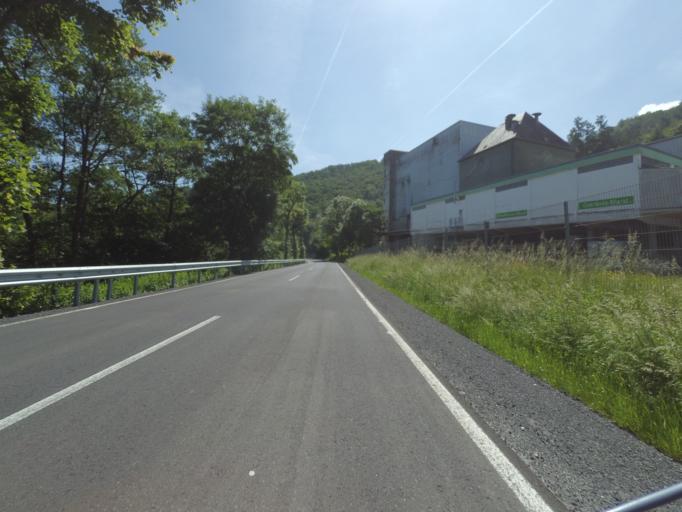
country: DE
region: Rheinland-Pfalz
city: Monreal
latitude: 50.2949
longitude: 7.1493
